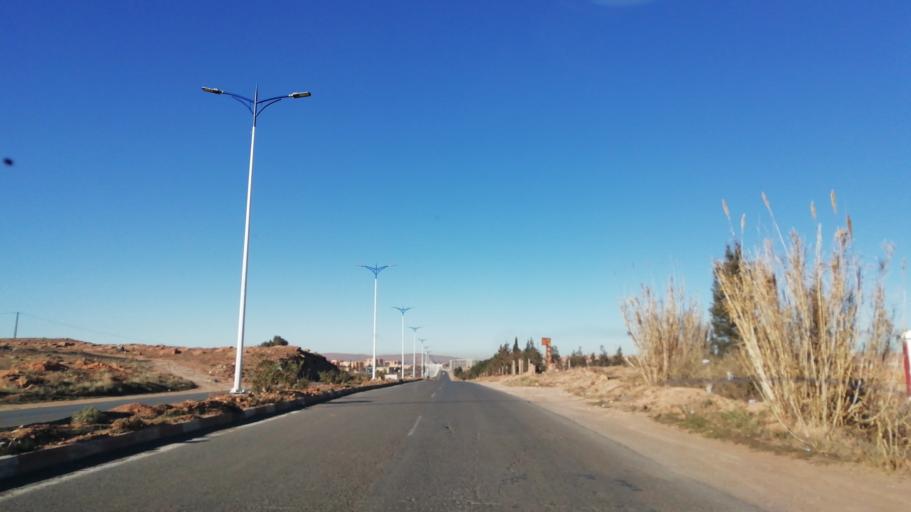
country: DZ
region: El Bayadh
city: El Bayadh
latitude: 33.6878
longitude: 1.0498
